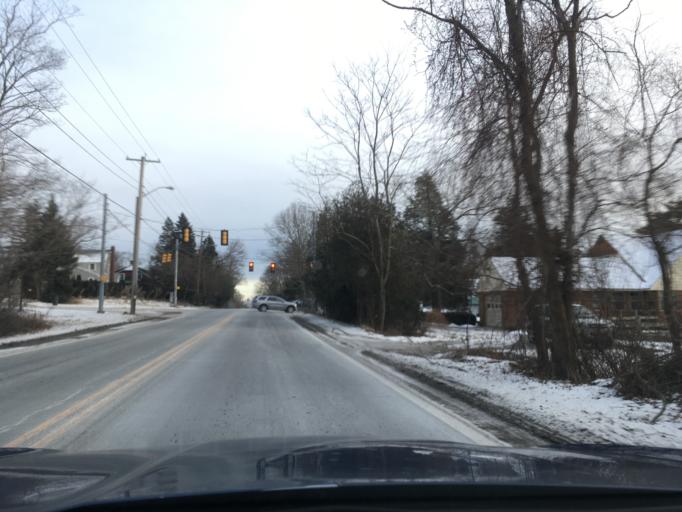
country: US
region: Rhode Island
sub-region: Kent County
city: East Greenwich
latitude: 41.6600
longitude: -71.4611
